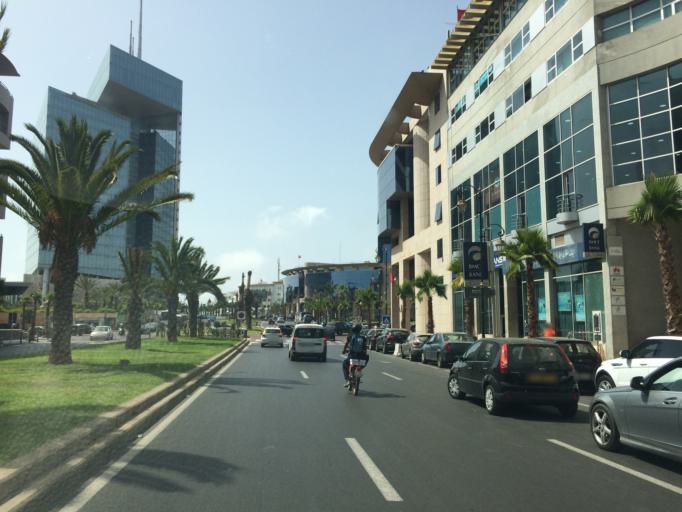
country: MA
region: Rabat-Sale-Zemmour-Zaer
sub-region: Skhirate-Temara
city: Temara
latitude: 33.9572
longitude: -6.8686
